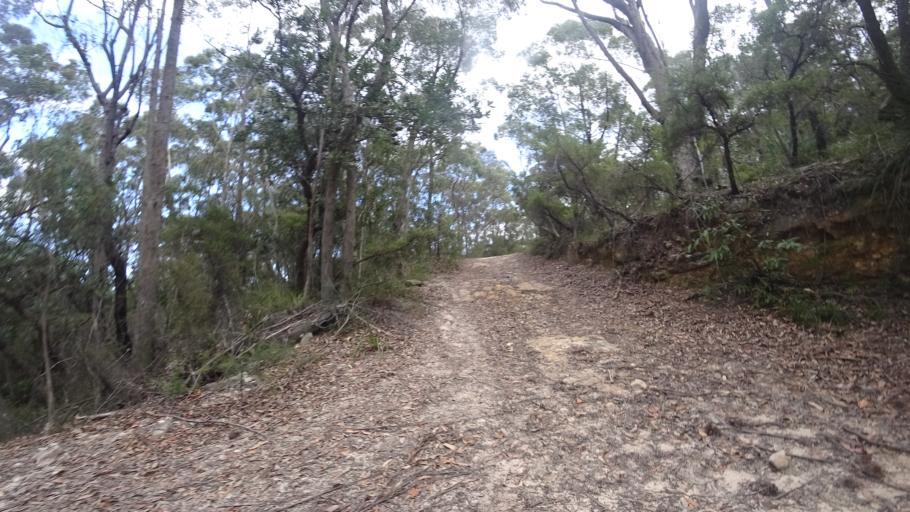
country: AU
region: New South Wales
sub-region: Warringah
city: Davidson
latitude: -33.6867
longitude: 151.1973
